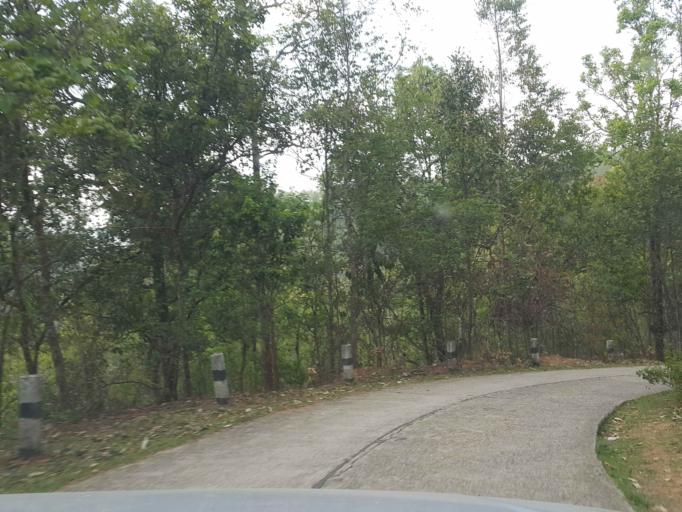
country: TH
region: Chiang Mai
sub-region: Amphoe Chiang Dao
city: Chiang Dao
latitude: 19.3851
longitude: 98.7715
